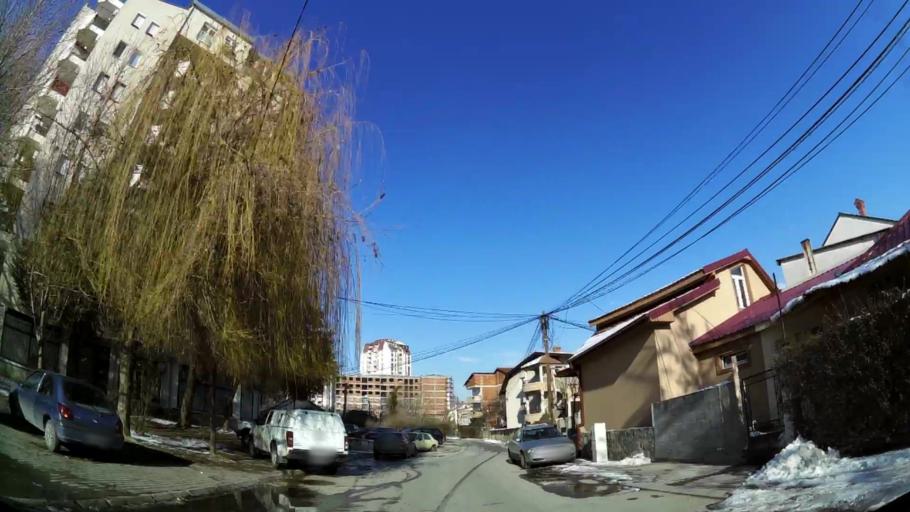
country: MK
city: Krushopek
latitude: 42.0031
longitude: 21.3806
